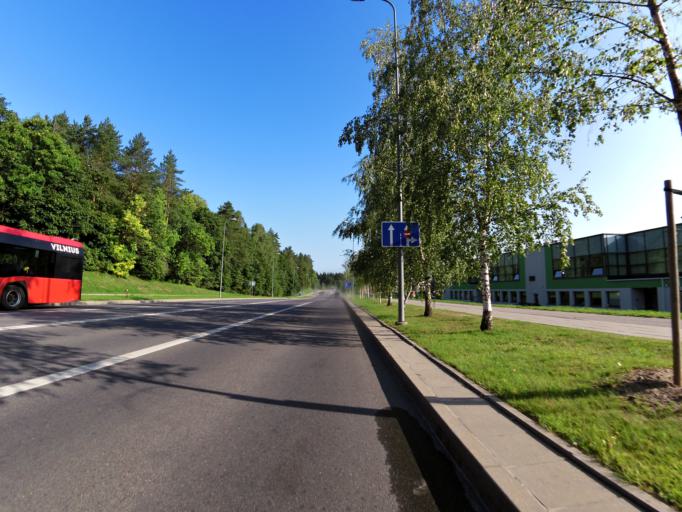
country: LT
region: Vilnius County
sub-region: Vilnius
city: Fabijoniskes
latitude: 54.7611
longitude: 25.2819
